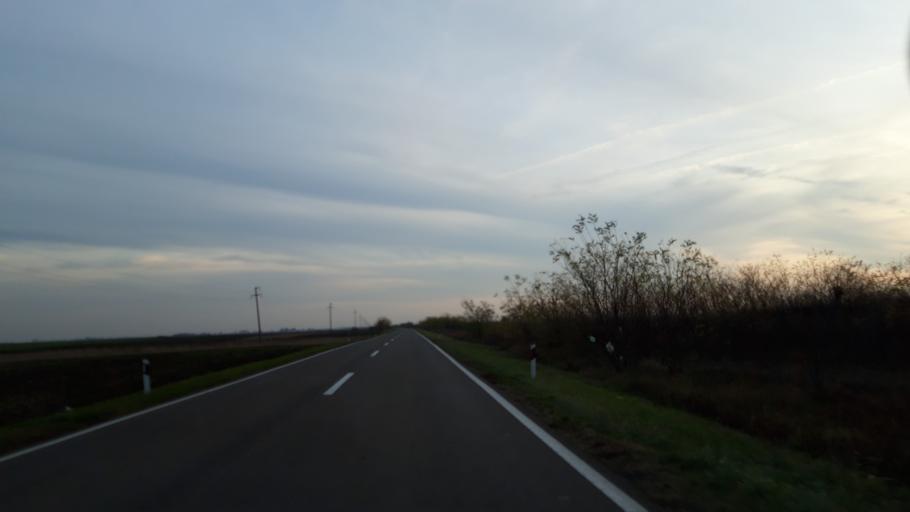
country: RS
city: Ostojicevo
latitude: 45.8660
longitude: 20.1648
